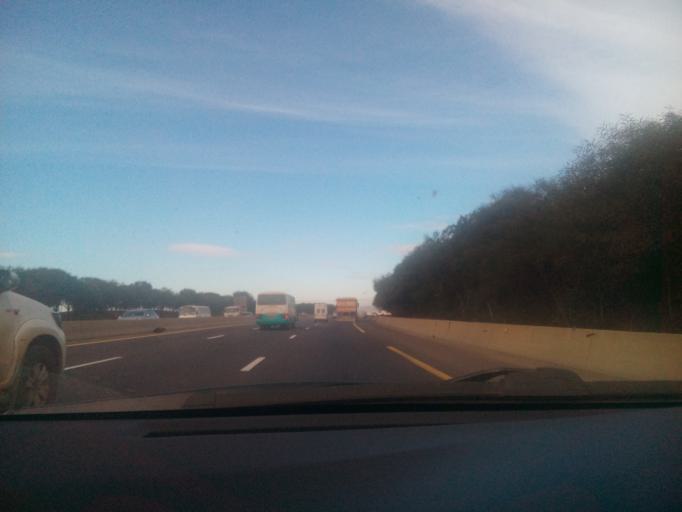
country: DZ
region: Oran
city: Es Senia
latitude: 35.5798
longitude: -0.5684
